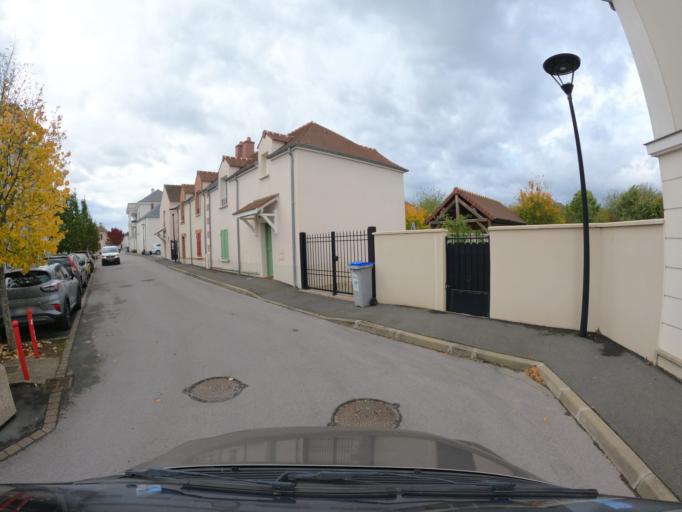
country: FR
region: Ile-de-France
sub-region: Departement de Seine-et-Marne
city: Magny-le-Hongre
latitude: 48.8717
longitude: 2.8114
